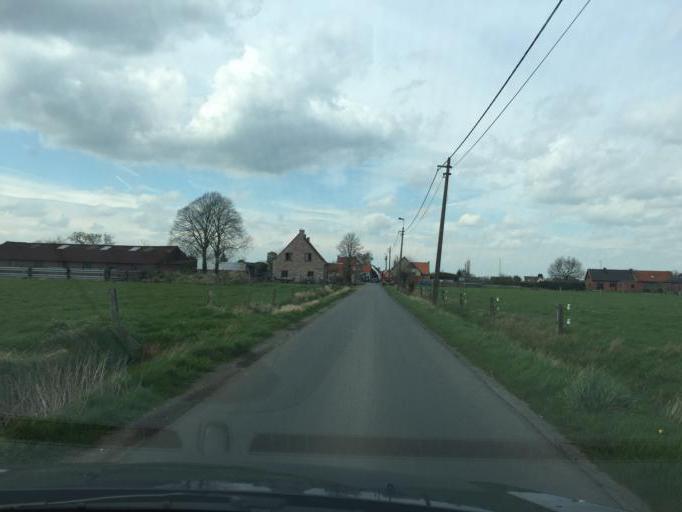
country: BE
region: Flanders
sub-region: Provincie Oost-Vlaanderen
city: Aalter
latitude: 51.0692
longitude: 3.4417
